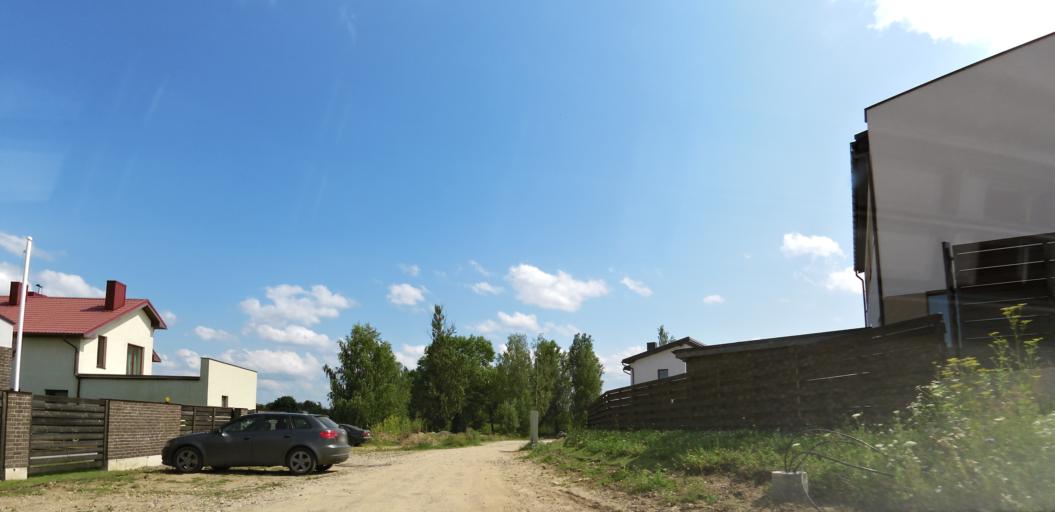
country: LT
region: Vilnius County
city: Pilaite
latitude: 54.7156
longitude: 25.1657
